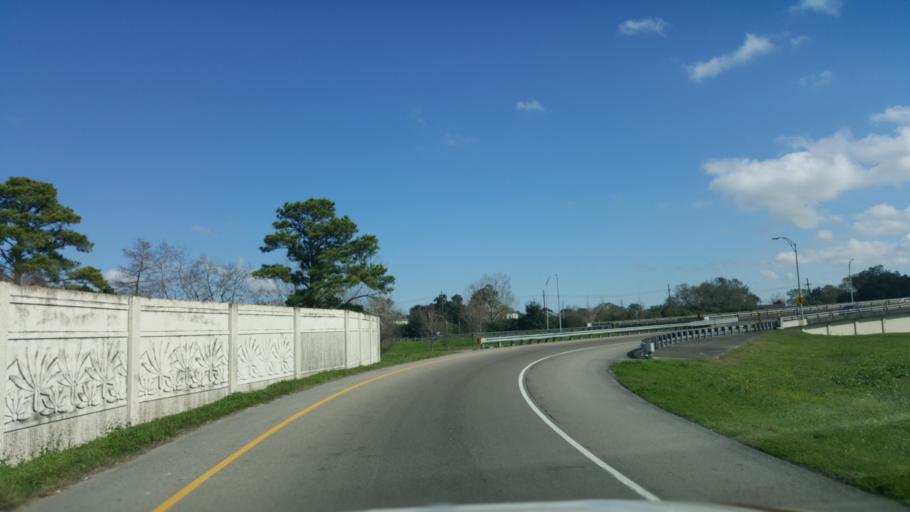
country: US
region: Louisiana
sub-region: Jefferson Parish
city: Metairie
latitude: 29.9972
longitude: -90.1170
